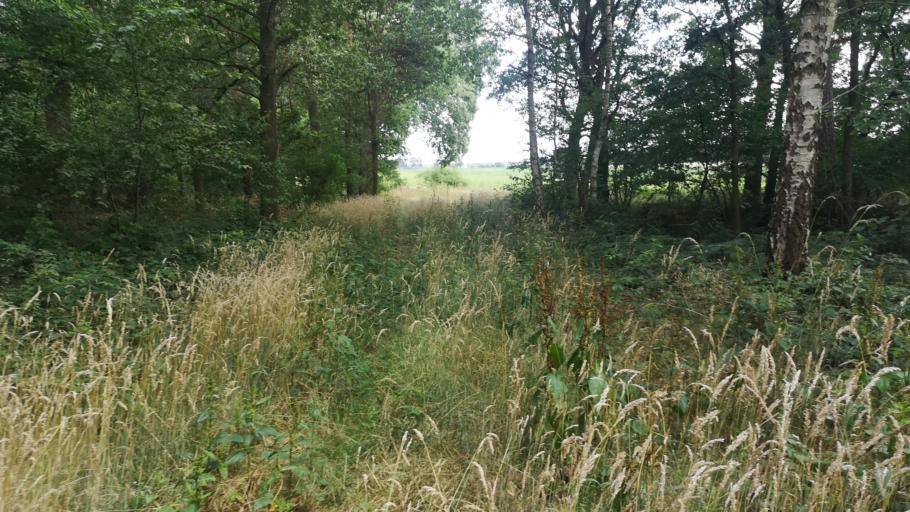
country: DE
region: Lower Saxony
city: Dahlem
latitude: 53.2359
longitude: 10.7461
